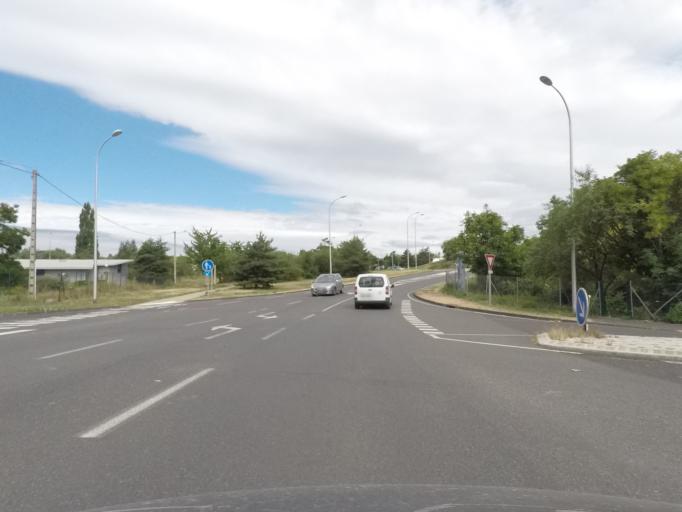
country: FR
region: Auvergne
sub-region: Departement du Puy-de-Dome
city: Beaumont
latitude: 45.7466
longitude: 3.0939
